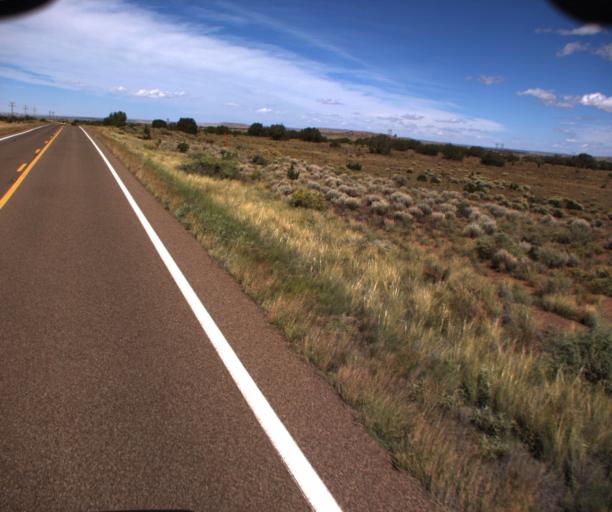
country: US
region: Arizona
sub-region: Apache County
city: Saint Johns
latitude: 34.5278
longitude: -109.6203
